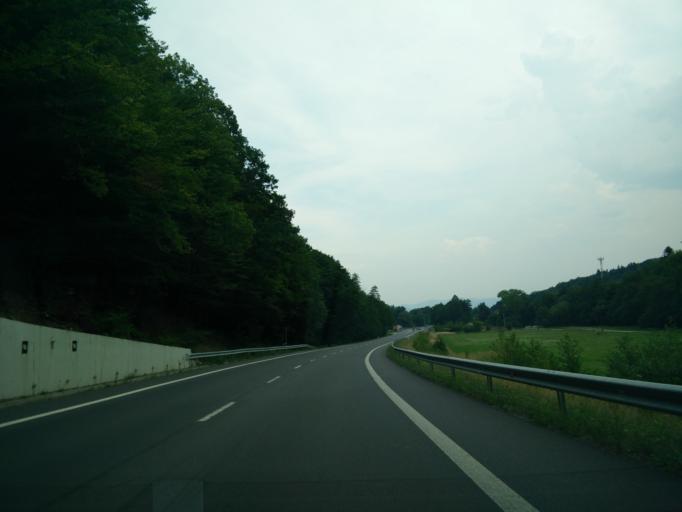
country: SK
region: Nitriansky
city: Handlova
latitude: 48.6540
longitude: 18.7495
